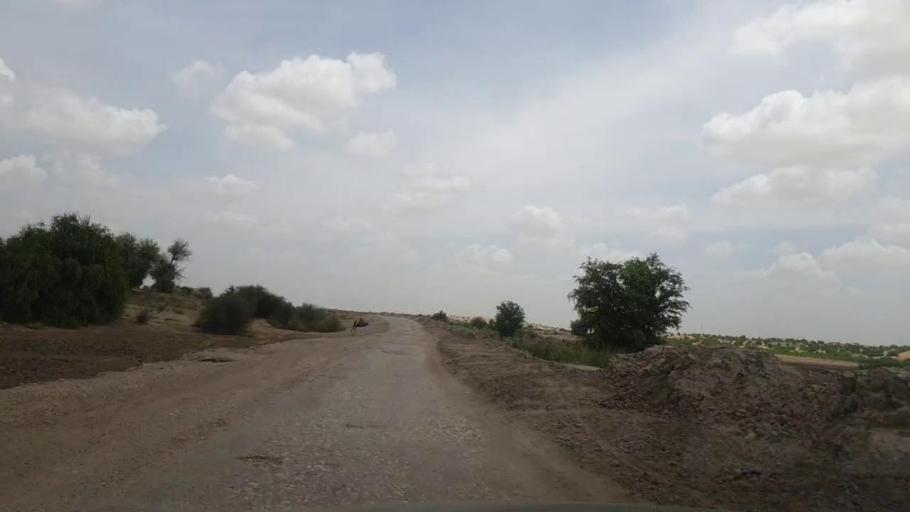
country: PK
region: Sindh
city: Kot Diji
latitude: 27.2017
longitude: 69.1225
